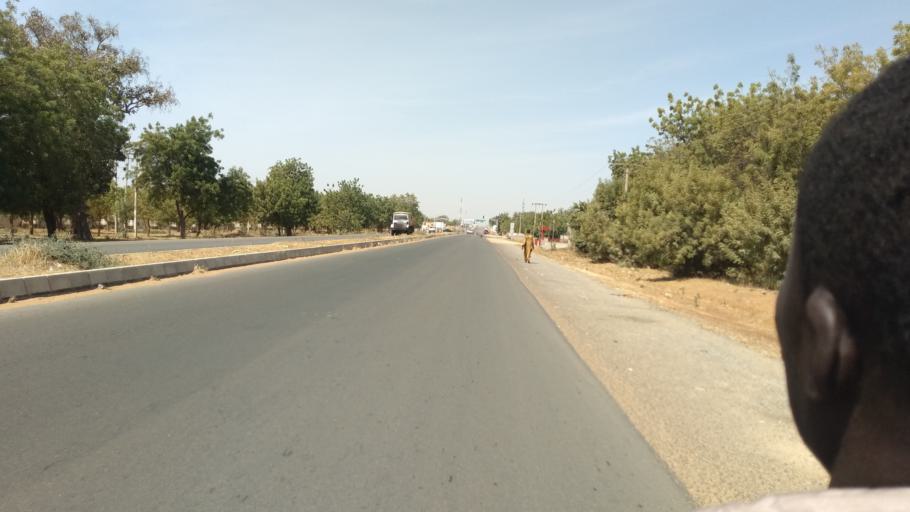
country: NG
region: Jigawa
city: Dutse
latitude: 11.6825
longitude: 9.3399
